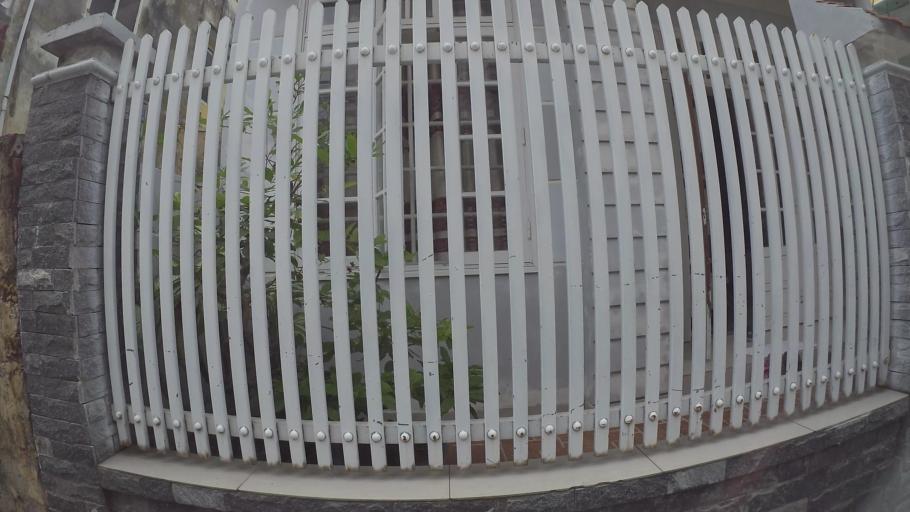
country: VN
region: Da Nang
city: Lien Chieu
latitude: 16.0716
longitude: 108.1518
